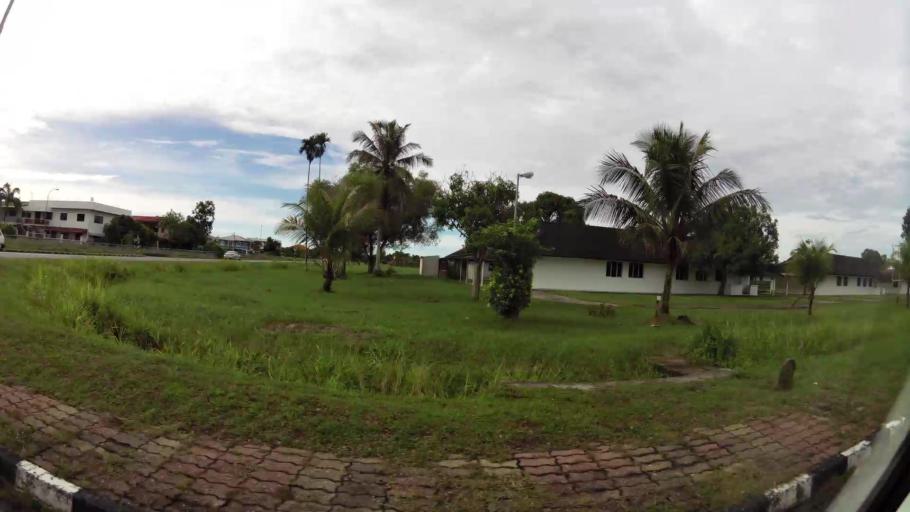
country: BN
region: Belait
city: Seria
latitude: 4.6107
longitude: 114.3271
